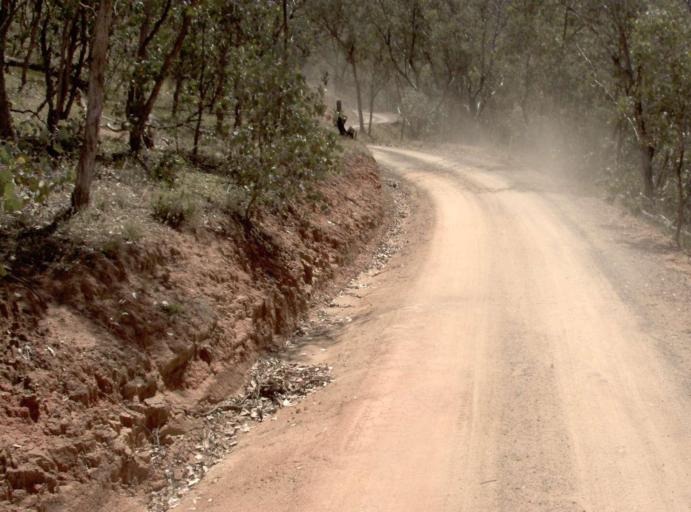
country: AU
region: New South Wales
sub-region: Snowy River
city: Jindabyne
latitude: -37.0942
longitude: 148.3708
